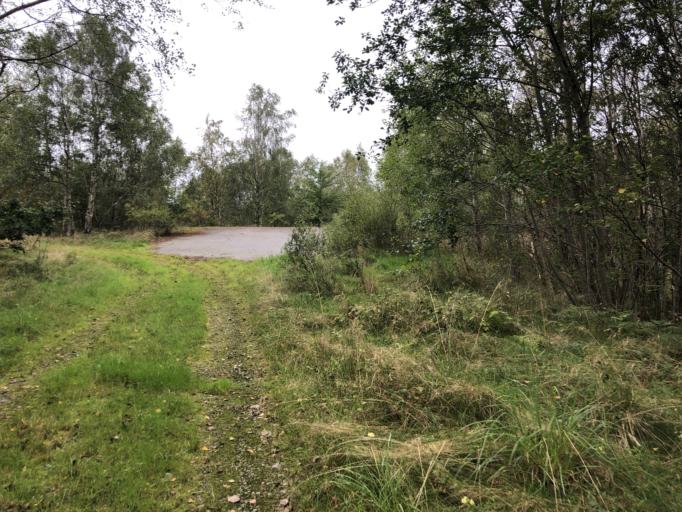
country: SE
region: Vaestra Goetaland
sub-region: Goteborg
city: Majorna
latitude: 57.7294
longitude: 11.8691
